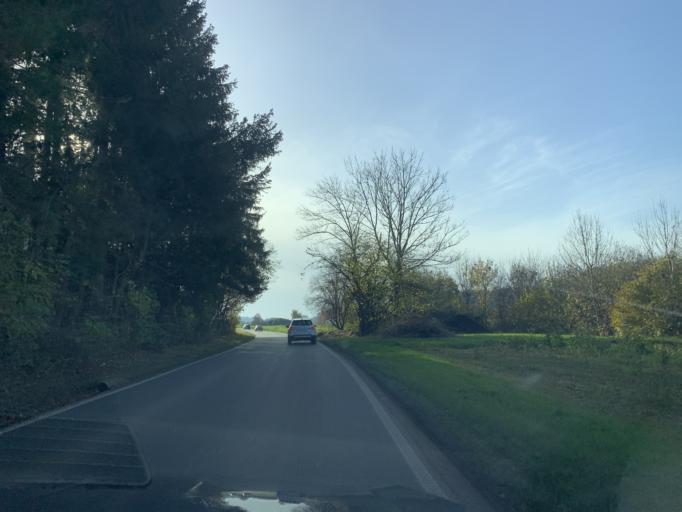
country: DE
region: Baden-Wuerttemberg
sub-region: Regierungsbezirk Stuttgart
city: Unterensingen
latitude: 48.6504
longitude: 9.3393
